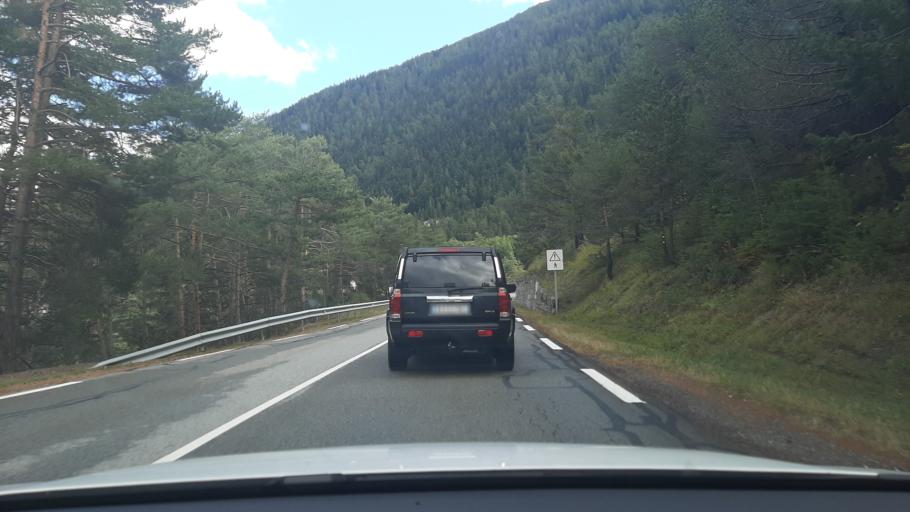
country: FR
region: Rhone-Alpes
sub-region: Departement de la Savoie
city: Modane
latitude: 45.2088
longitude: 6.7315
